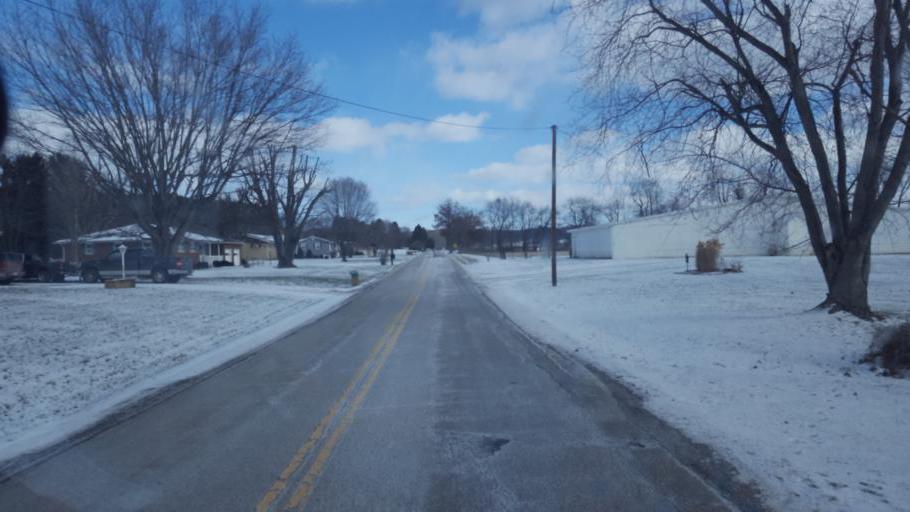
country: US
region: Ohio
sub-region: Coshocton County
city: Coshocton
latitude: 40.3122
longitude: -81.8234
